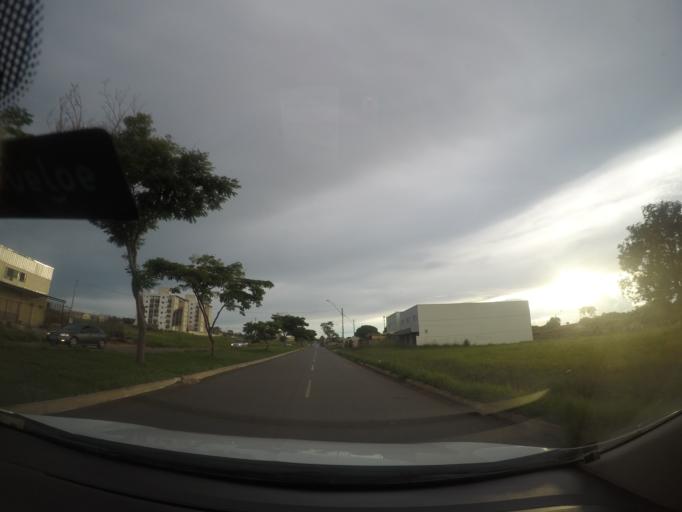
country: BR
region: Goias
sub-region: Goiania
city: Goiania
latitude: -16.7429
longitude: -49.3158
